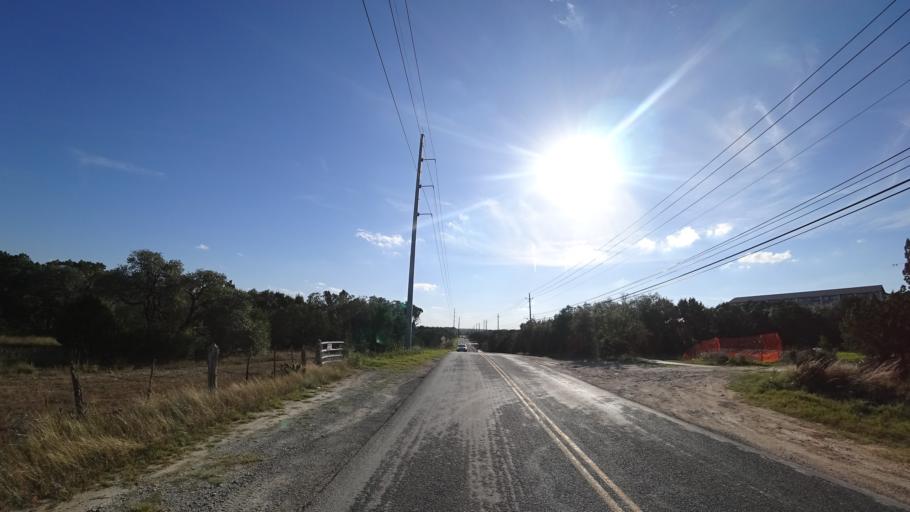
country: US
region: Texas
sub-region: Travis County
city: Barton Creek
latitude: 30.2469
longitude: -97.8545
